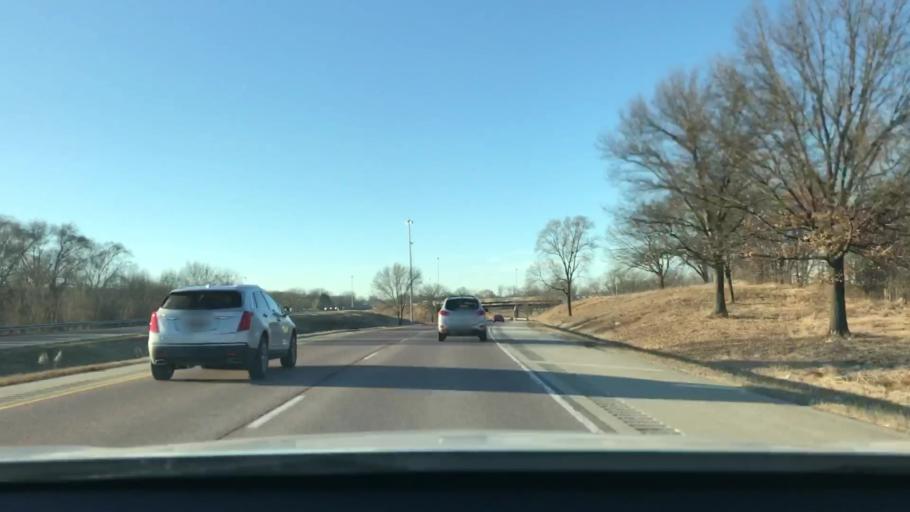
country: US
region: Illinois
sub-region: Kane County
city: Elgin
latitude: 42.0301
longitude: -88.3316
